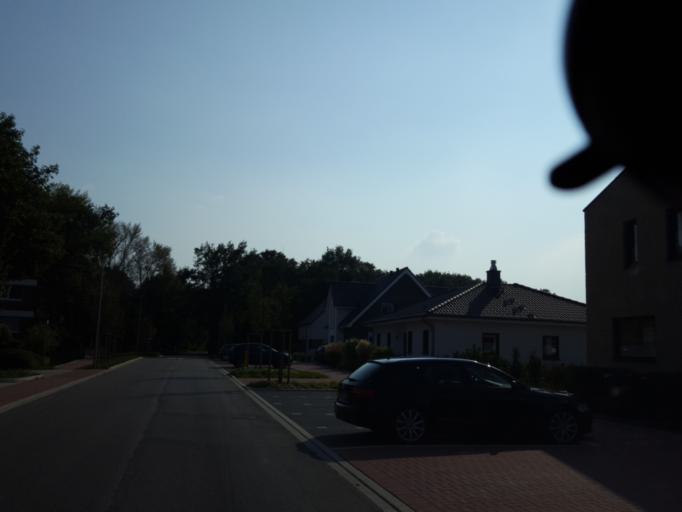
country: DE
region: North Rhine-Westphalia
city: Dorsten
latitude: 51.6792
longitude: 6.9315
